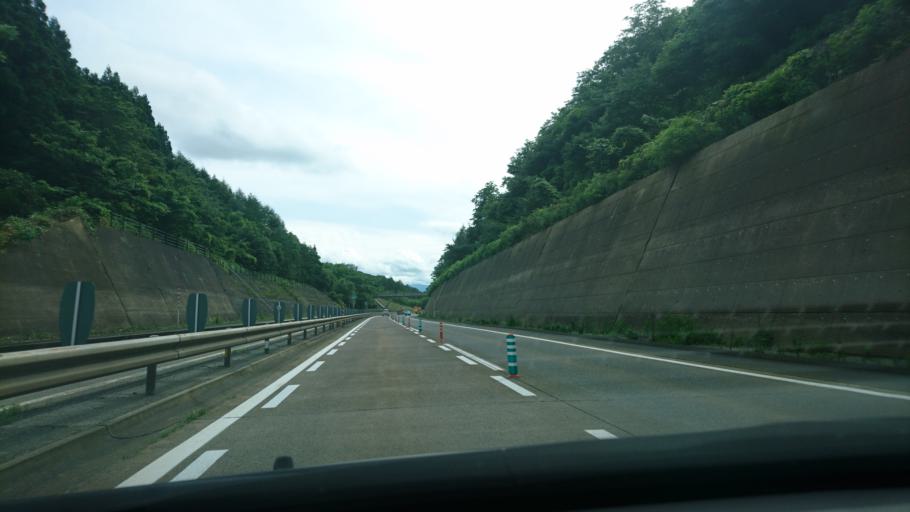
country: JP
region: Iwate
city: Ichinohe
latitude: 40.2277
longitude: 141.3697
